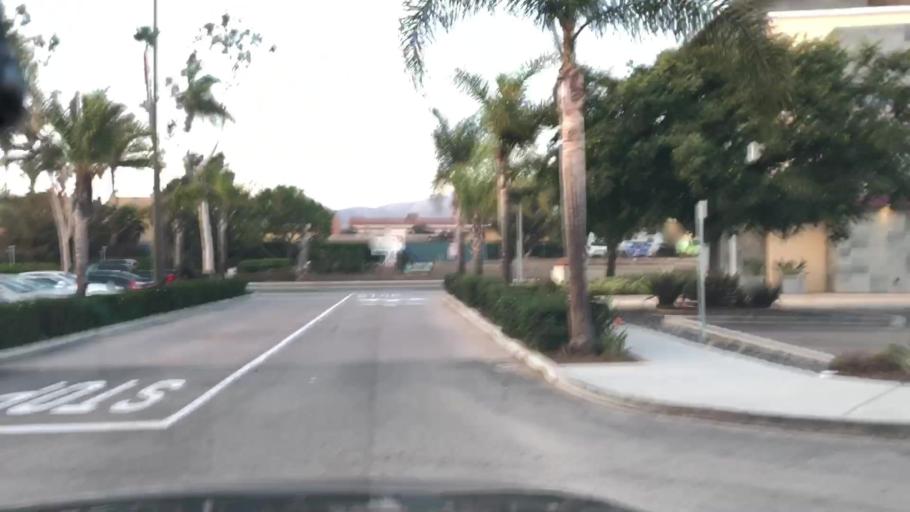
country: US
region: California
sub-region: Ventura County
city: Ventura
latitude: 34.2669
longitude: -119.2452
